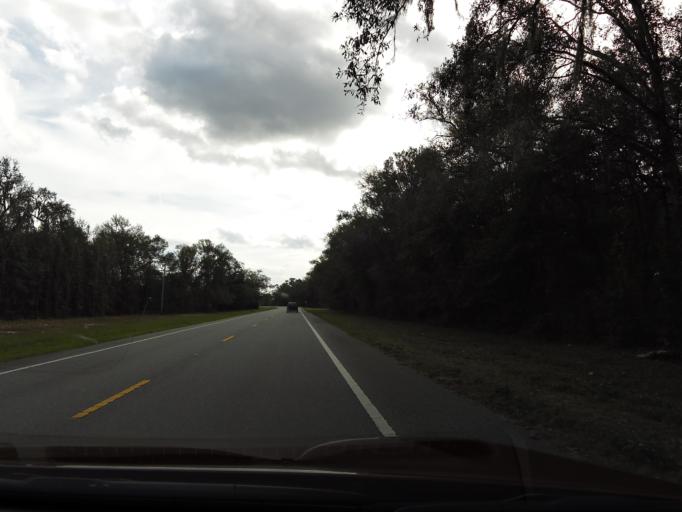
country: US
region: Florida
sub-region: Volusia County
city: De Leon Springs
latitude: 29.2343
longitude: -81.3246
